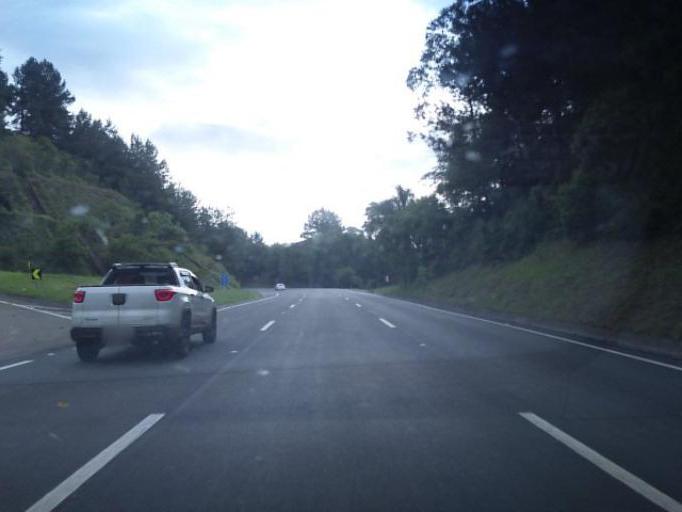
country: BR
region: Parana
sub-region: Campina Grande Do Sul
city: Campina Grande do Sul
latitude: -25.1830
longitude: -48.8847
